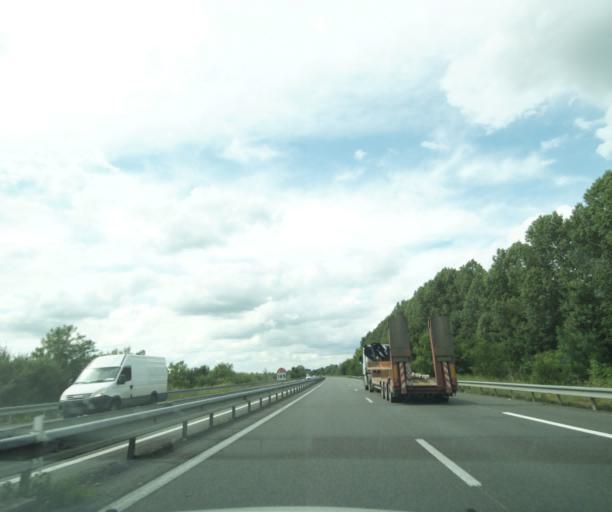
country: FR
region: Centre
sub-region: Departement du Cher
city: Foecy
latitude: 47.1779
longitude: 2.1764
